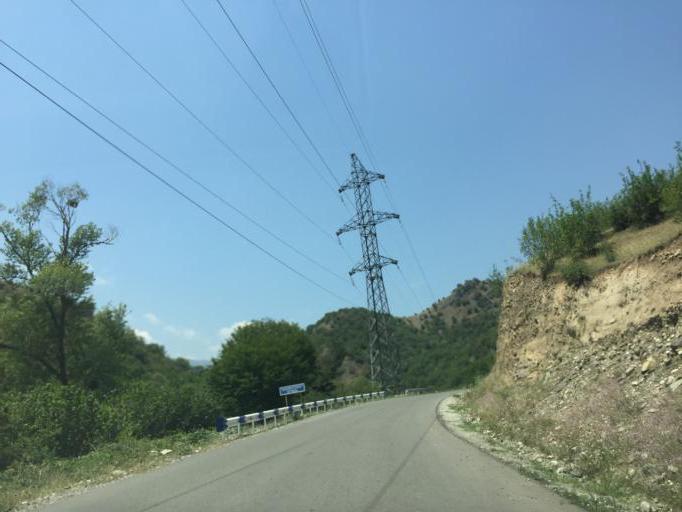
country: AZ
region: Kalbacar Rayonu
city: Kerbakhiar
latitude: 40.1334
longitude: 46.3799
